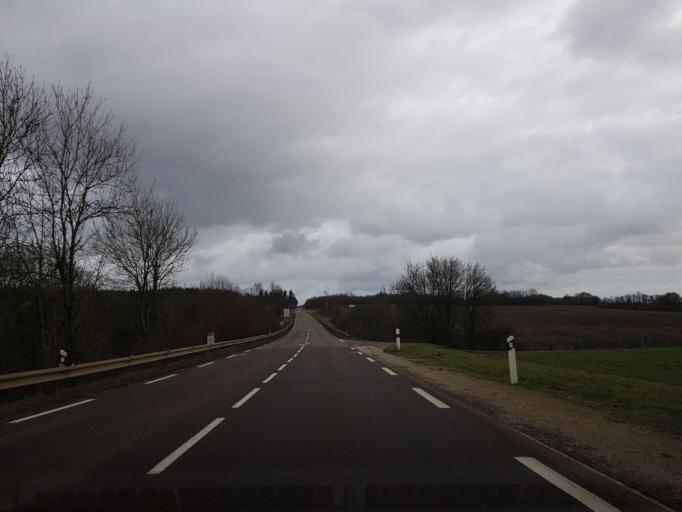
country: FR
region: Franche-Comte
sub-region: Departement de la Haute-Saone
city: Scey-sur-Saone-et-Saint-Albin
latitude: 47.7005
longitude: 5.9484
